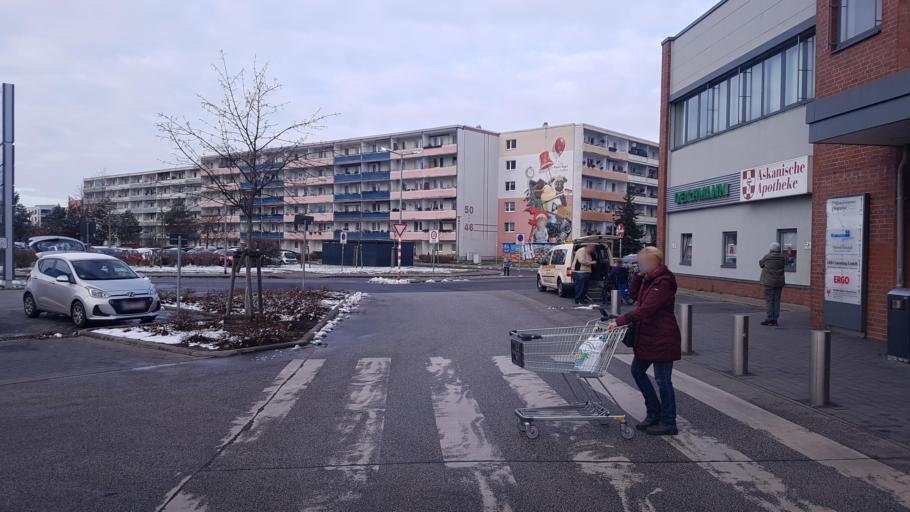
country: DE
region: Brandenburg
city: Strausberg
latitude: 52.5734
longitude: 13.8967
